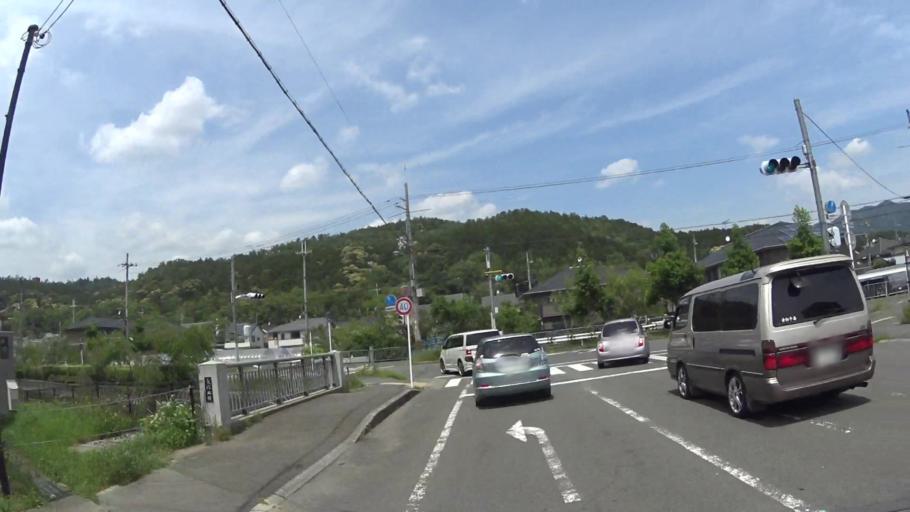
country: JP
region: Kyoto
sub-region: Kyoto-shi
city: Kamigyo-ku
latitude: 35.0695
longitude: 135.7775
